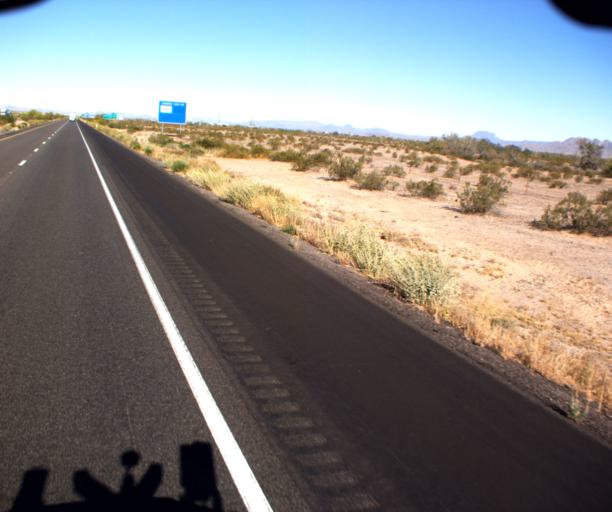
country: US
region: Arizona
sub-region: Maricopa County
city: Gila Bend
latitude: 32.9212
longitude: -112.6519
